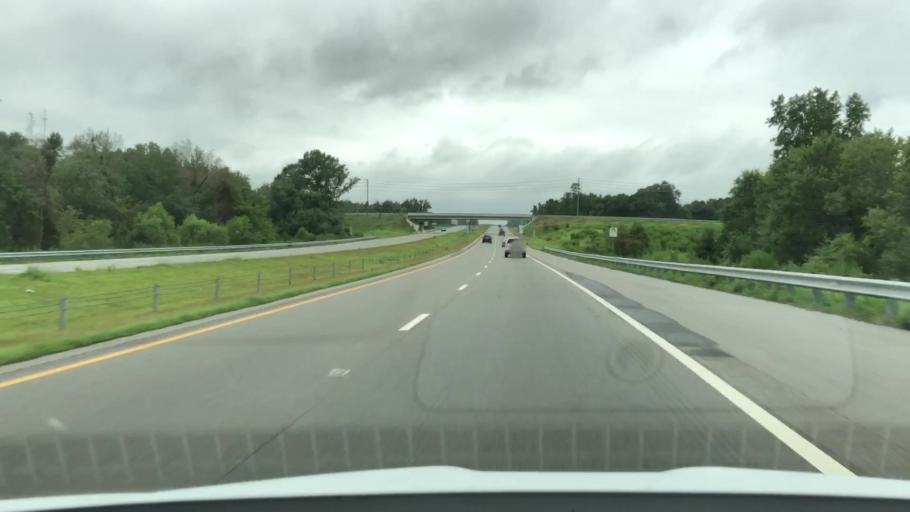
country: US
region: North Carolina
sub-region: Lenoir County
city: La Grange
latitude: 35.3092
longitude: -77.8224
